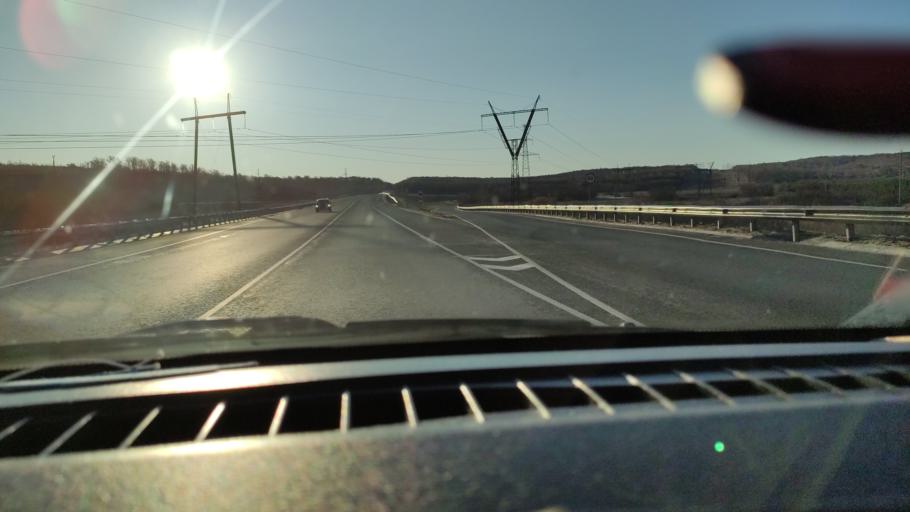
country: RU
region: Saratov
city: Shikhany
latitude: 52.1148
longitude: 47.3014
